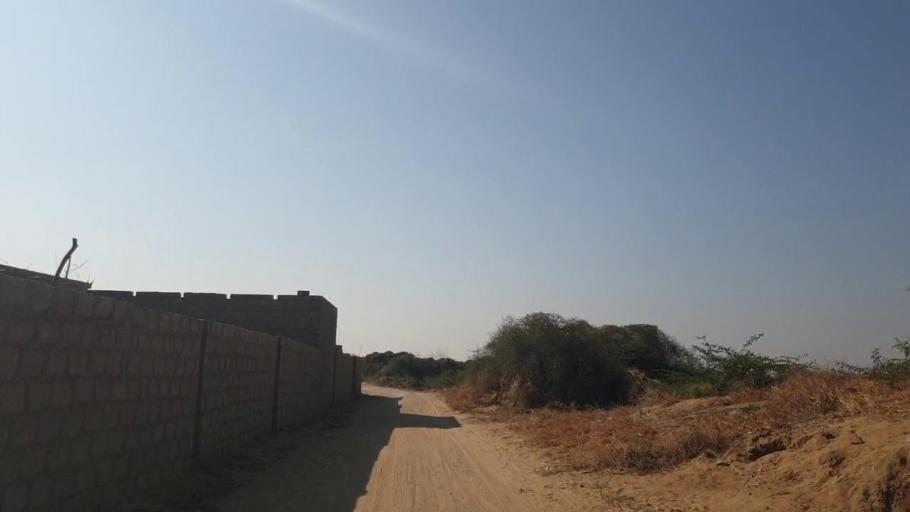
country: PK
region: Sindh
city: Thatta
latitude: 25.1271
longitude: 67.7734
